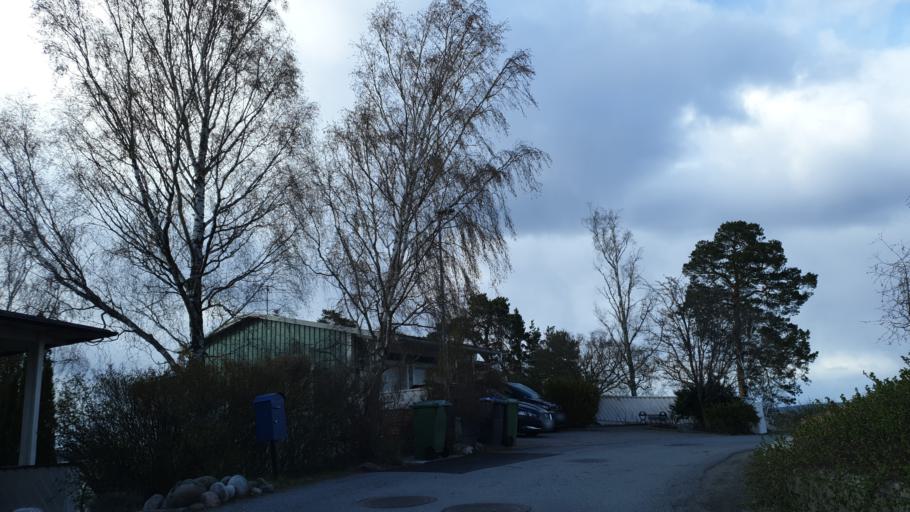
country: SE
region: Stockholm
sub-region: Lidingo
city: Lidingoe
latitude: 59.3908
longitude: 18.1168
